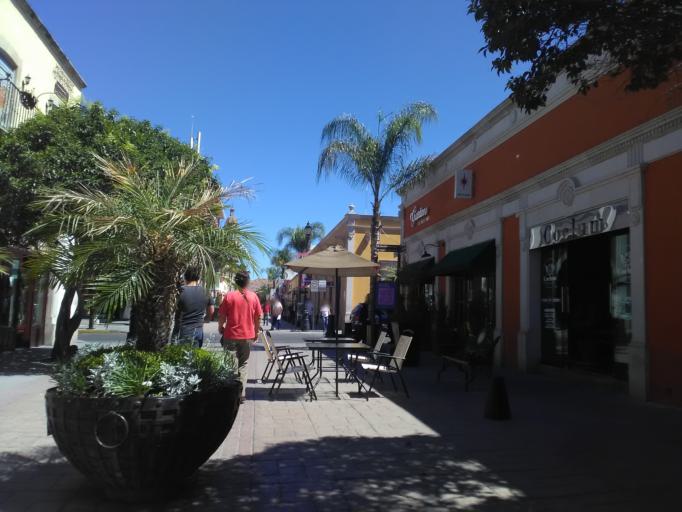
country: MX
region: Durango
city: Victoria de Durango
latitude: 24.0282
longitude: -104.6709
